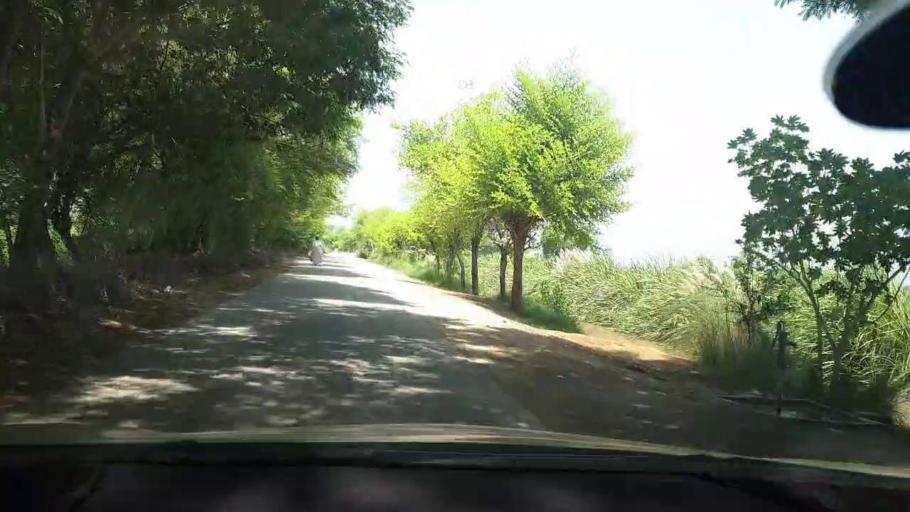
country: PK
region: Sindh
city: Kambar
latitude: 27.6415
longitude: 67.9739
